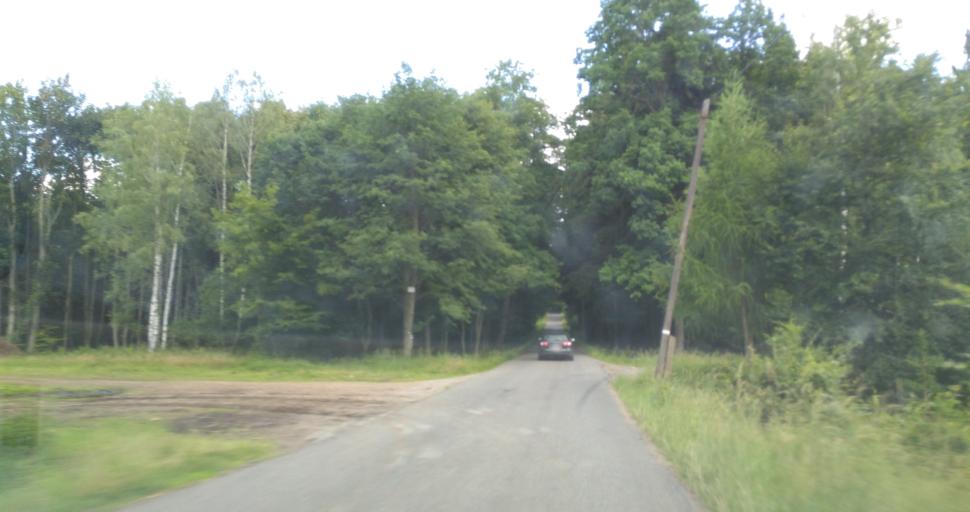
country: CZ
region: Plzensky
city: Zbiroh
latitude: 49.9046
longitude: 13.8152
